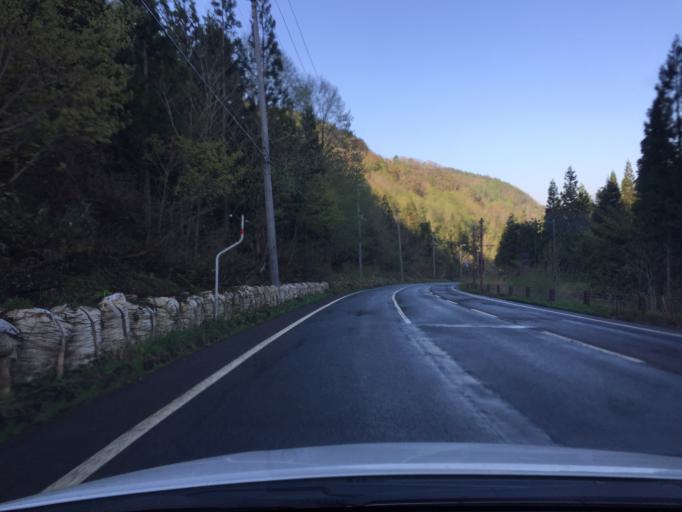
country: JP
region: Fukushima
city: Inawashiro
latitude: 37.6617
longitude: 140.0273
